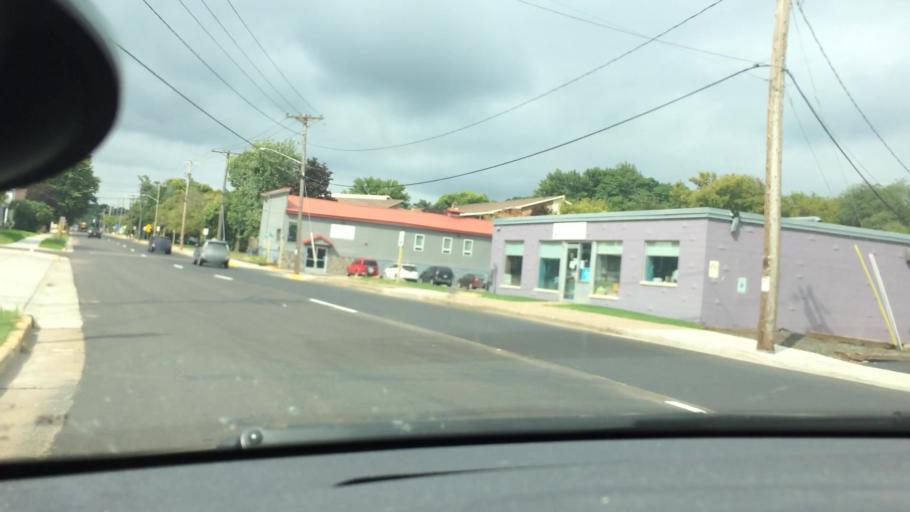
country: US
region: Wisconsin
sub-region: Chippewa County
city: Chippewa Falls
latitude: 44.9393
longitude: -91.3923
